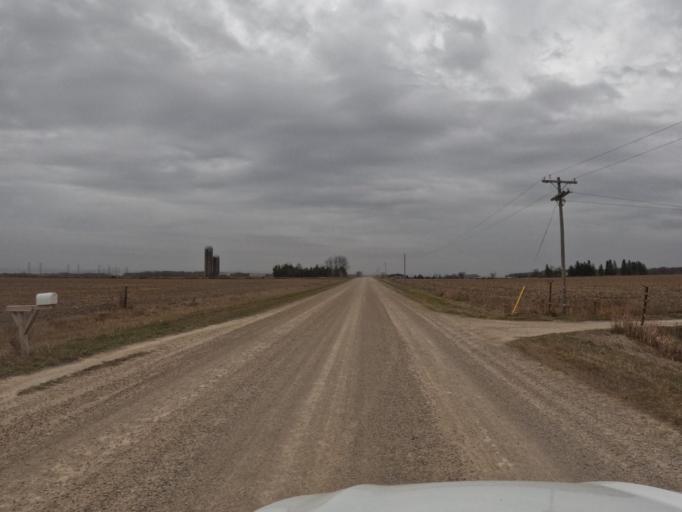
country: CA
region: Ontario
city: Shelburne
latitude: 43.8858
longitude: -80.3591
